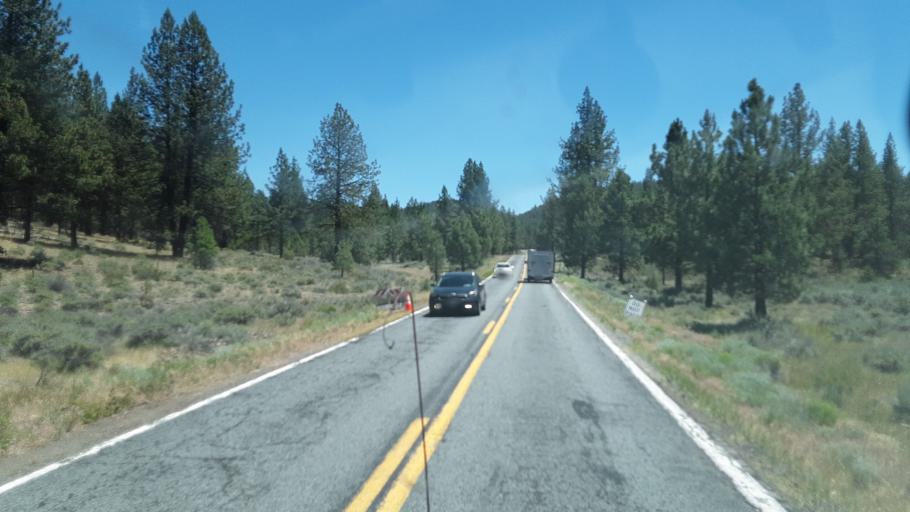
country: US
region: California
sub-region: Modoc County
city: Alturas
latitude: 40.9854
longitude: -120.7970
